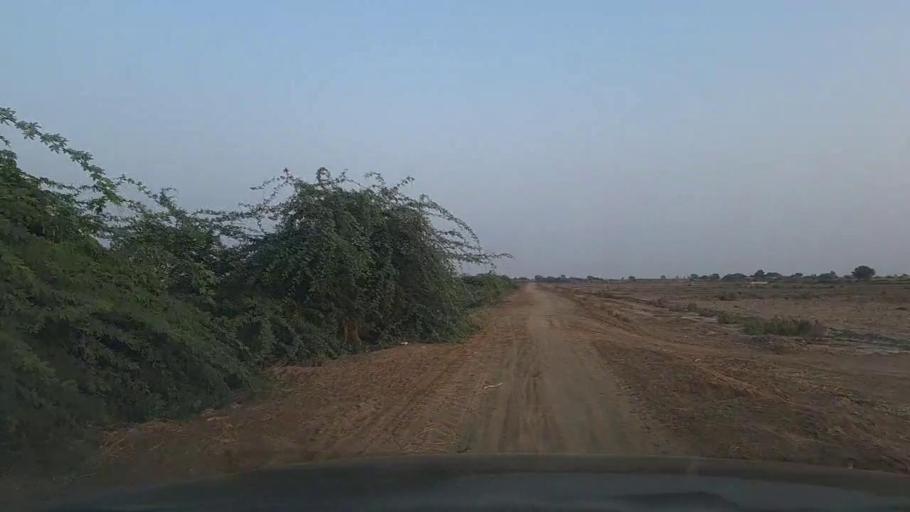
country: PK
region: Sindh
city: Jati
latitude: 24.5417
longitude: 68.3978
